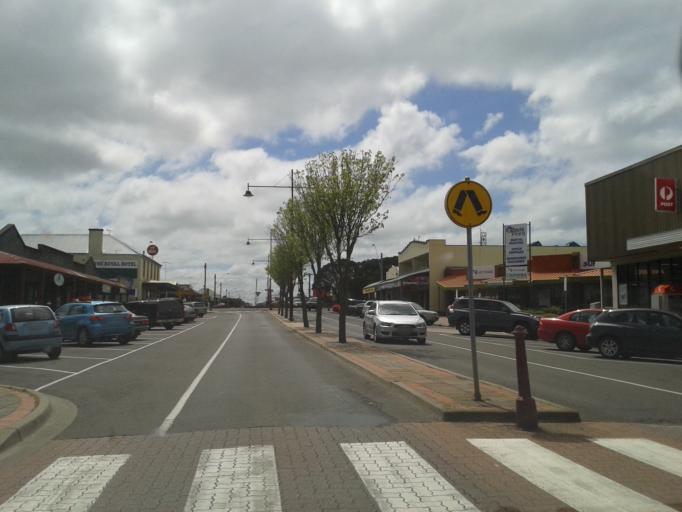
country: AU
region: Victoria
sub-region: Glenelg
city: Portland
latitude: -38.3453
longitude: 141.6038
